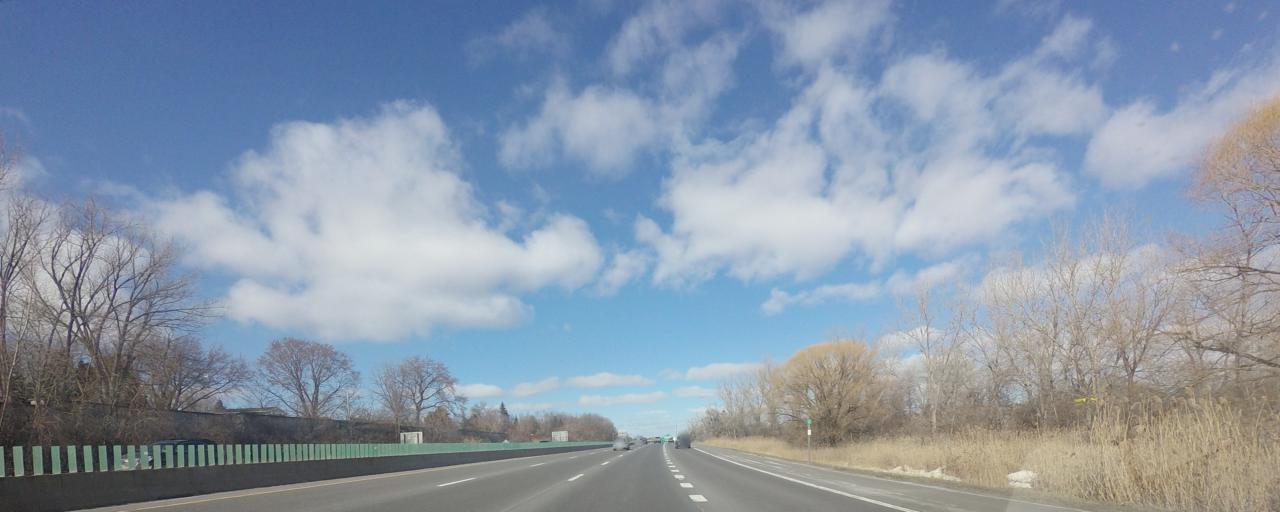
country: US
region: New York
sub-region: Onondaga County
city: Galeville
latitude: 43.0841
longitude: -76.1713
